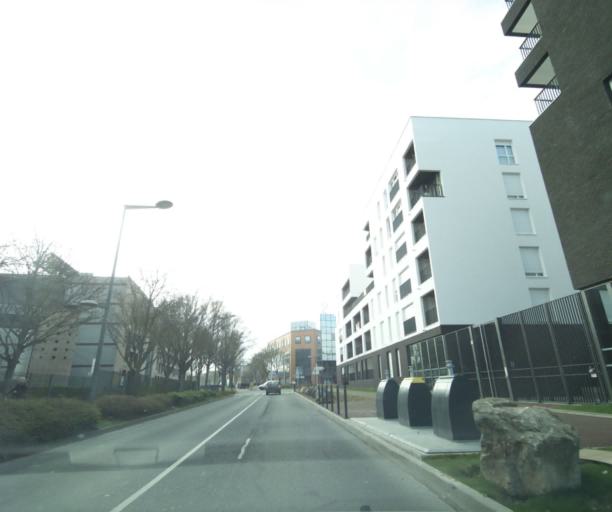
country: FR
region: Ile-de-France
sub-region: Departement du Val-d'Oise
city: Vaureal
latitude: 49.0509
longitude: 2.0376
